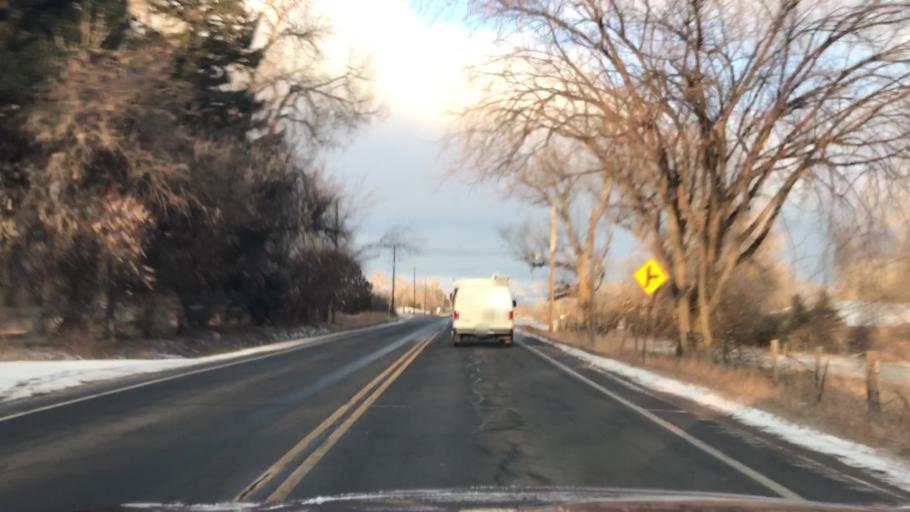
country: US
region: Colorado
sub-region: Boulder County
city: Louisville
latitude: 40.0147
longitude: -105.1445
